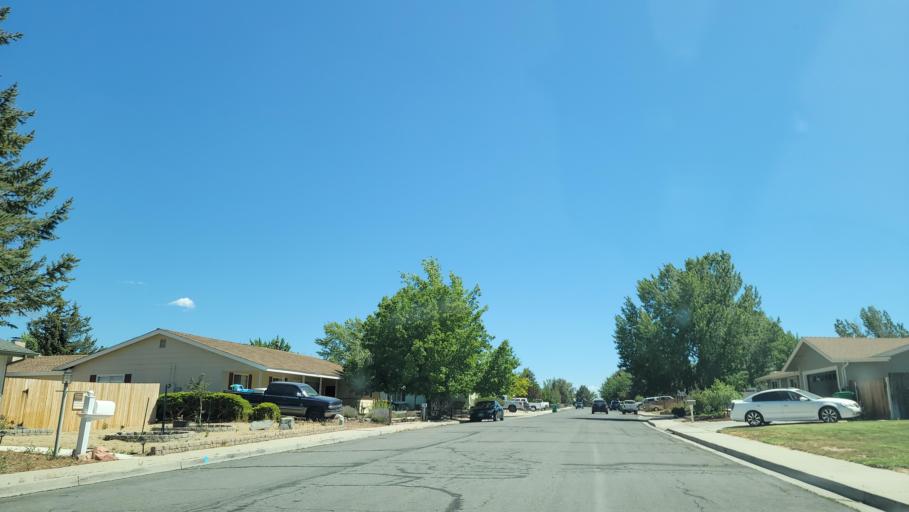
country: US
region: Nevada
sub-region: Carson City
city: Carson City
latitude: 39.1392
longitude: -119.7551
